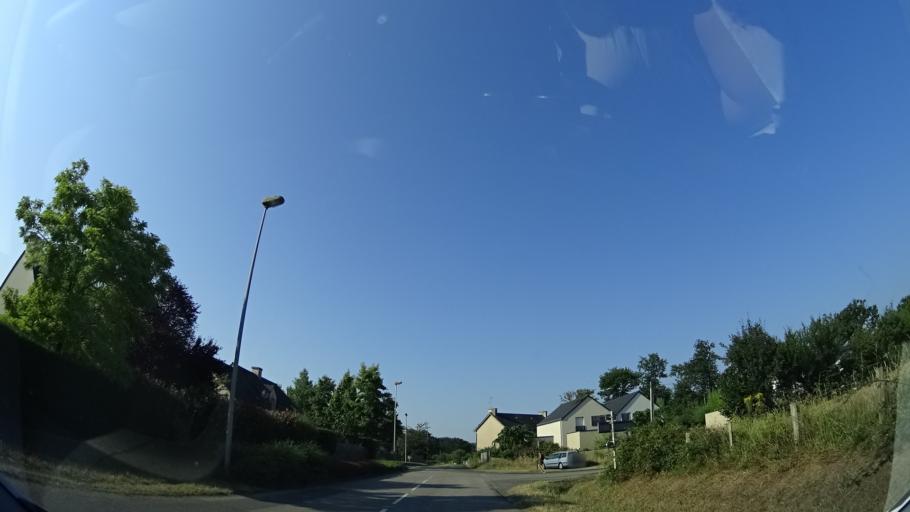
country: FR
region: Brittany
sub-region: Departement d'Ille-et-Vilaine
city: Pace
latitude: 48.1539
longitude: -1.7922
